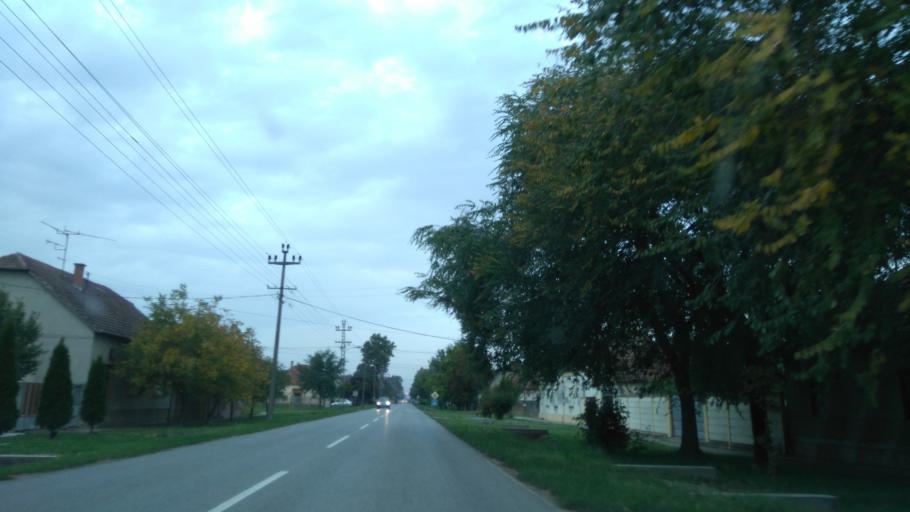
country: RS
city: Mol
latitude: 45.7589
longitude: 20.1302
